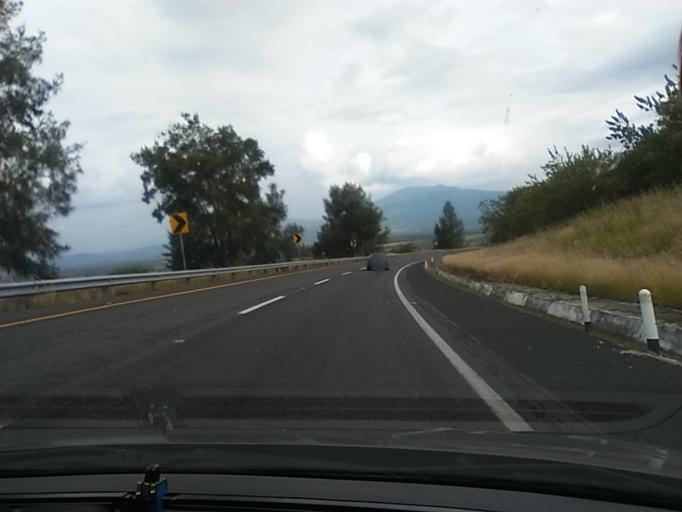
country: MX
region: Michoacan
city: Ixtlan
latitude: 20.1918
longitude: -102.3130
